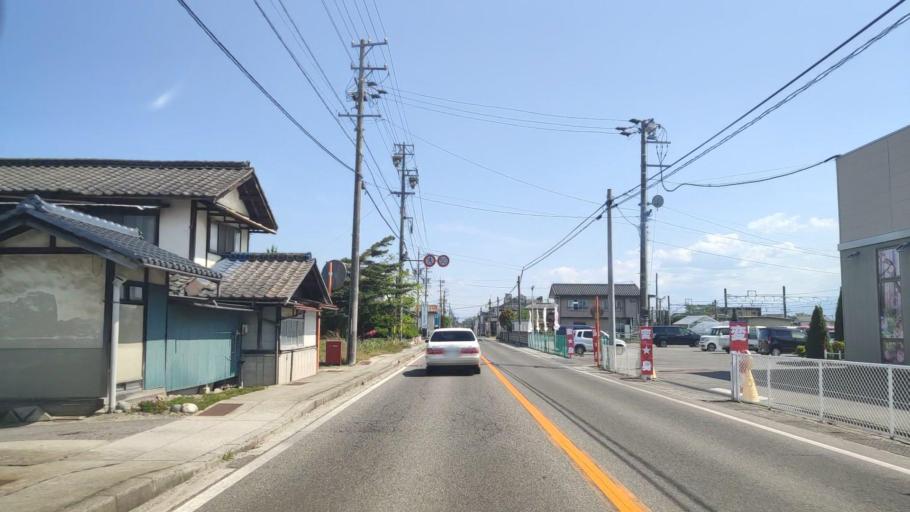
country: JP
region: Nagano
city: Hotaka
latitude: 36.3610
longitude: 137.8784
